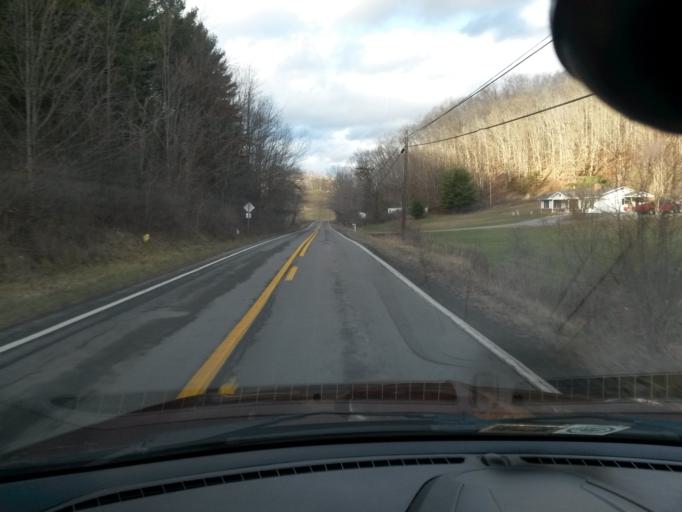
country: US
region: Virginia
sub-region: Giles County
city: Pembroke
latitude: 37.4635
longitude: -80.6604
